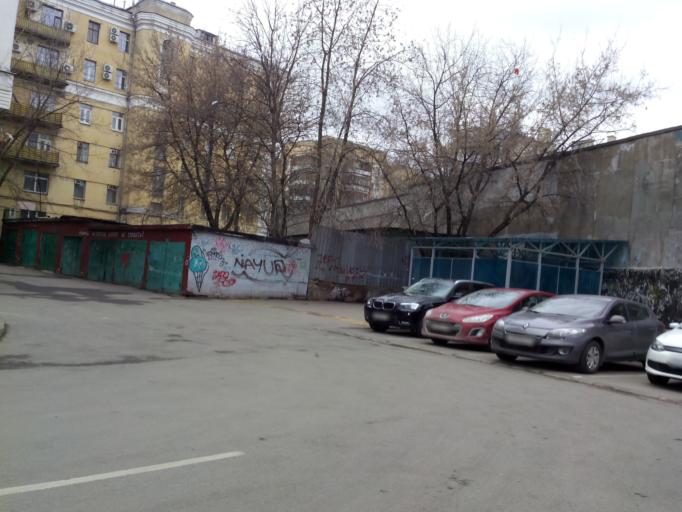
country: RU
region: Moskovskaya
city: Bogorodskoye
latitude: 55.7960
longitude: 37.6994
